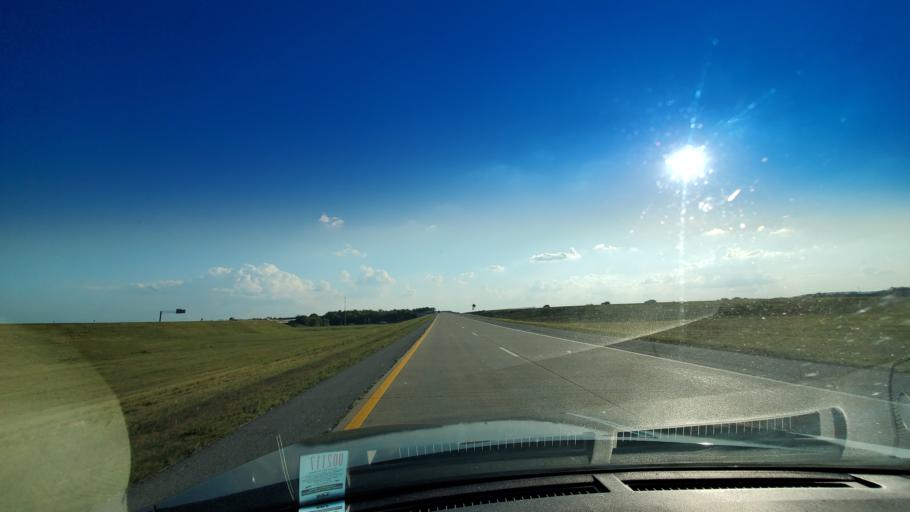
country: US
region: Tennessee
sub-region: Rutherford County
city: Murfreesboro
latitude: 35.8880
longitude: -86.4746
